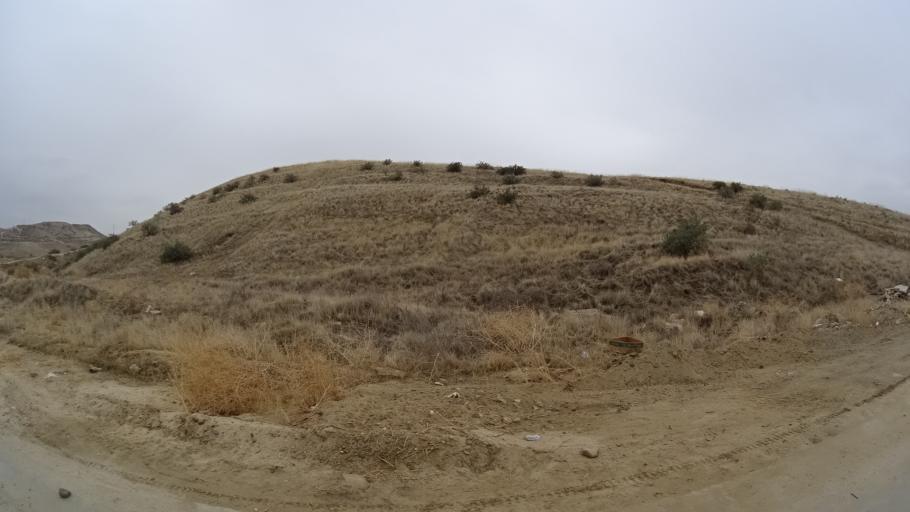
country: US
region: California
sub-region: Kern County
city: Oildale
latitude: 35.4241
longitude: -118.9422
